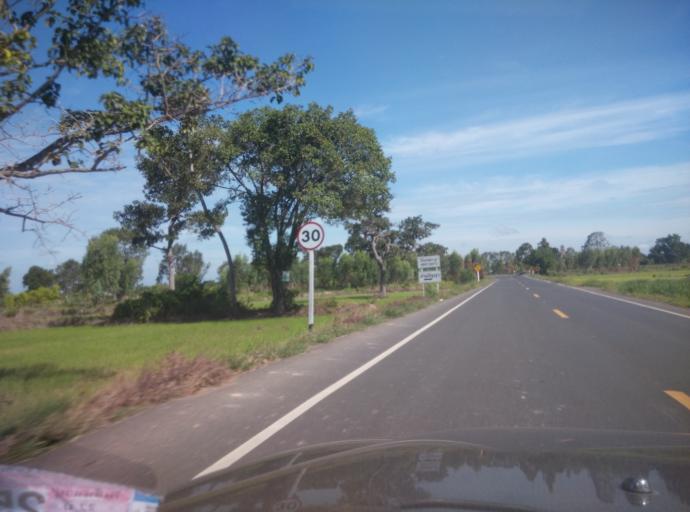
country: TH
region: Sisaket
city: Si Sa Ket
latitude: 15.1220
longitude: 104.2502
